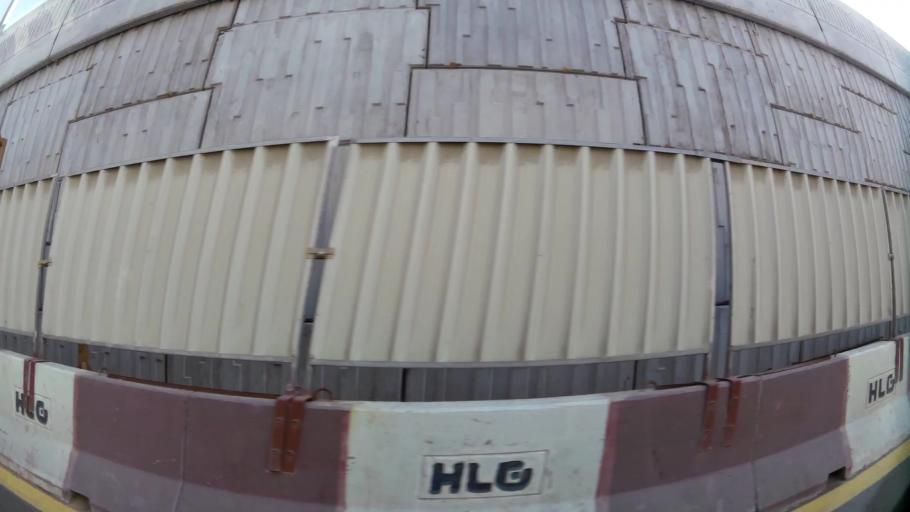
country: AE
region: Ash Shariqah
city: Sharjah
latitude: 25.2320
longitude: 55.3877
